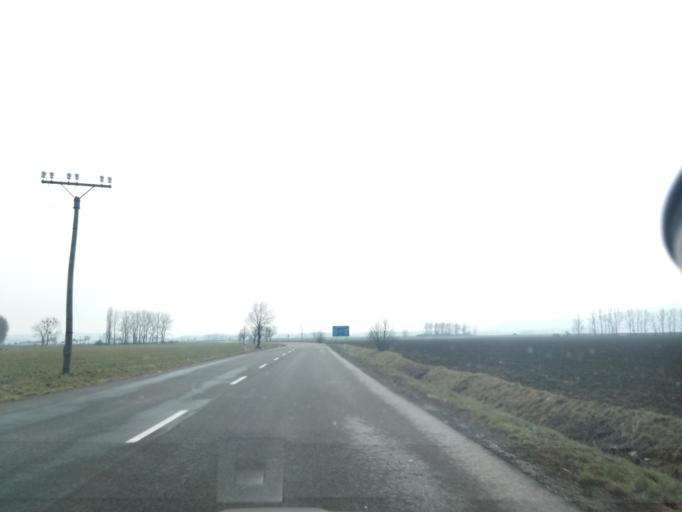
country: SK
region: Kosicky
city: Trebisov
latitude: 48.5510
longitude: 21.6850
